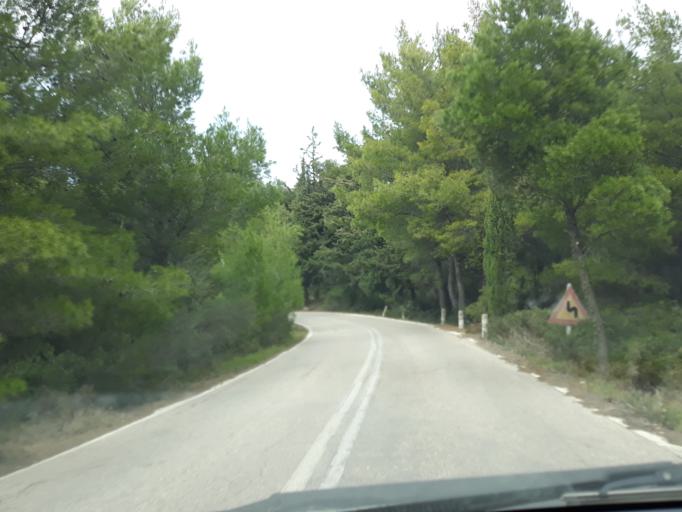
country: GR
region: Attica
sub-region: Nomarchia Anatolikis Attikis
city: Varybobi
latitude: 38.1411
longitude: 23.7936
